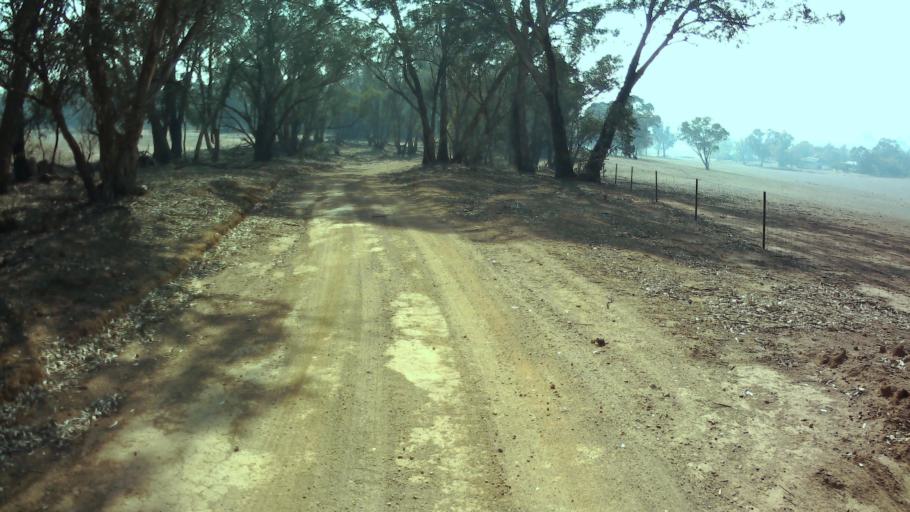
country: AU
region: New South Wales
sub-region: Weddin
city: Grenfell
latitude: -33.8959
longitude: 148.1800
